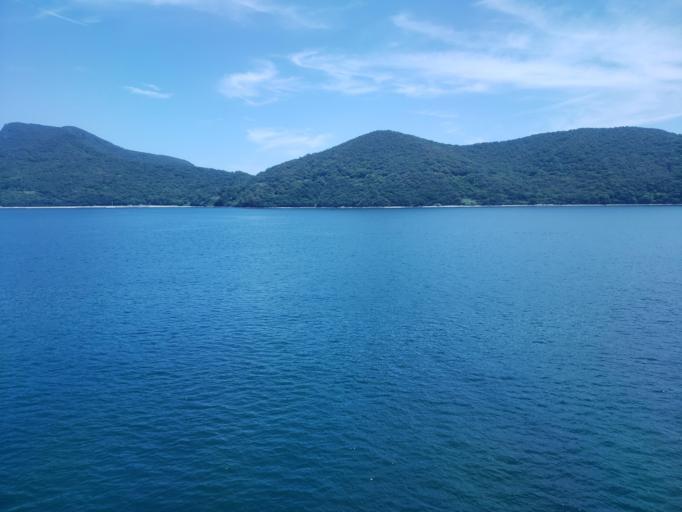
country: JP
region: Kagawa
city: Tonosho
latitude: 34.4360
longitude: 134.3210
